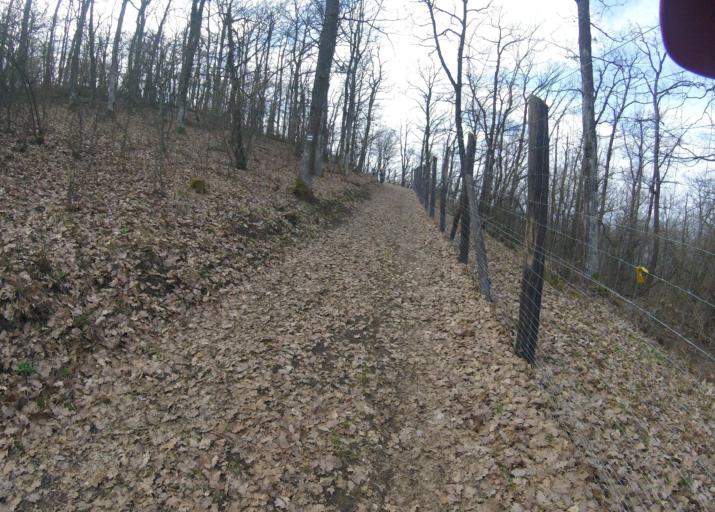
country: HU
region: Heves
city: Belapatfalva
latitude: 48.0086
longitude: 20.3404
